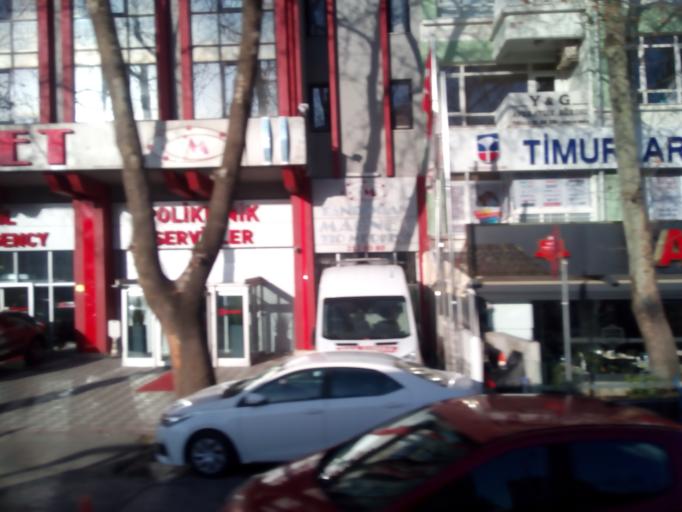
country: TR
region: Ankara
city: Ankara
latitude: 39.9344
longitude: 32.8376
